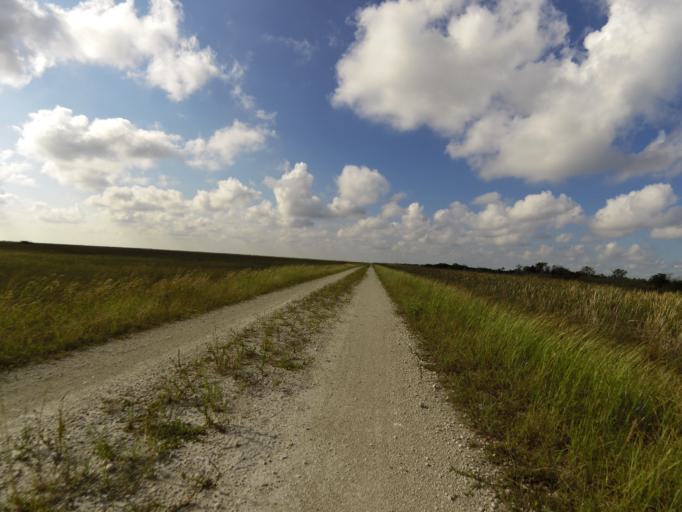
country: US
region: Florida
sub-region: Broward County
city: Weston
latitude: 26.0447
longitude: -80.4848
